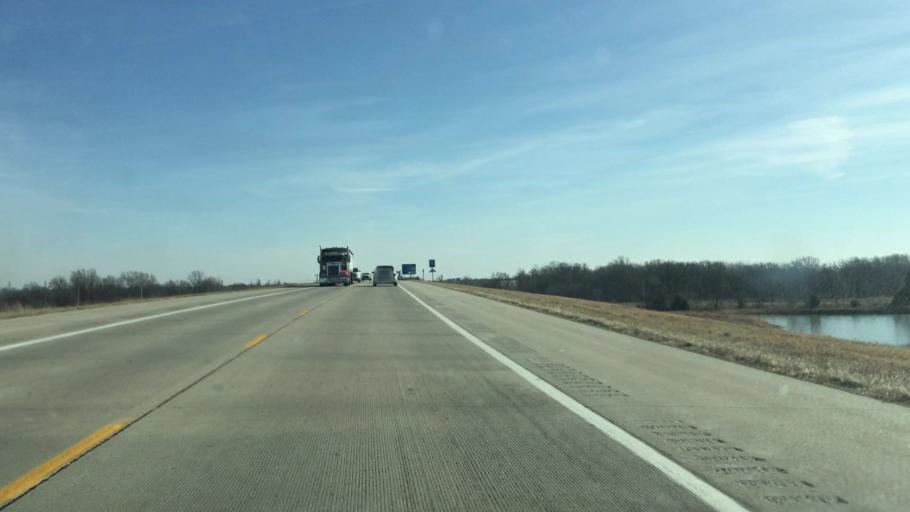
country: US
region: Kansas
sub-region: Labette County
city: Parsons
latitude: 37.3696
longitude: -95.2778
